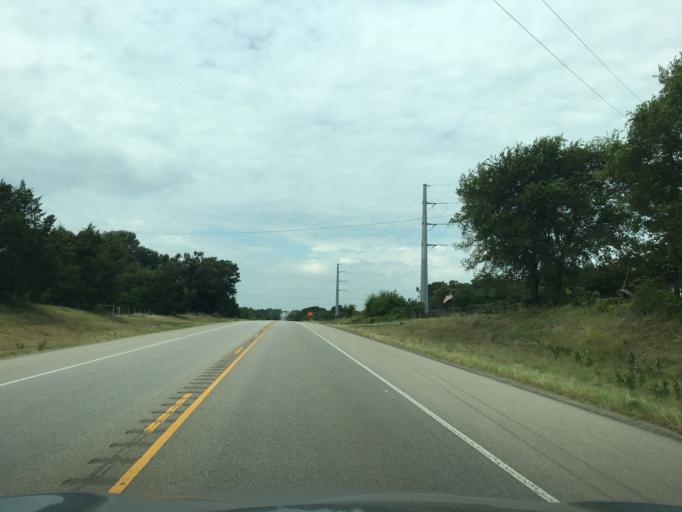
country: US
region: Texas
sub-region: Collin County
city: Anna
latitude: 33.3242
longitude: -96.4945
